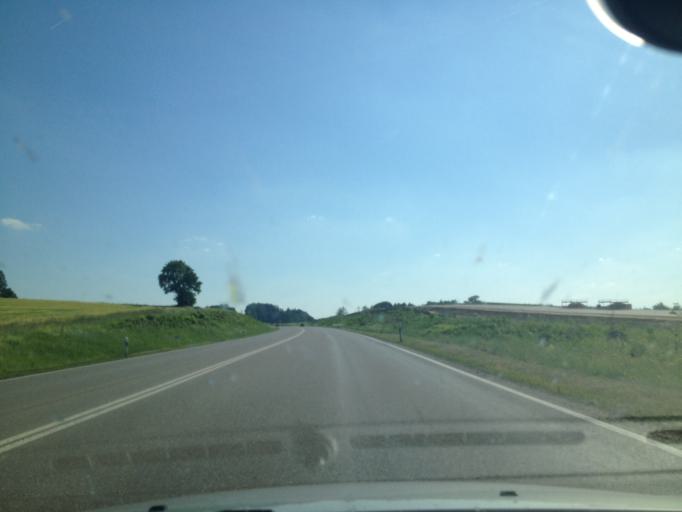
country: DE
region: Bavaria
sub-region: Swabia
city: Obergriesbach
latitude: 48.4271
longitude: 11.0975
